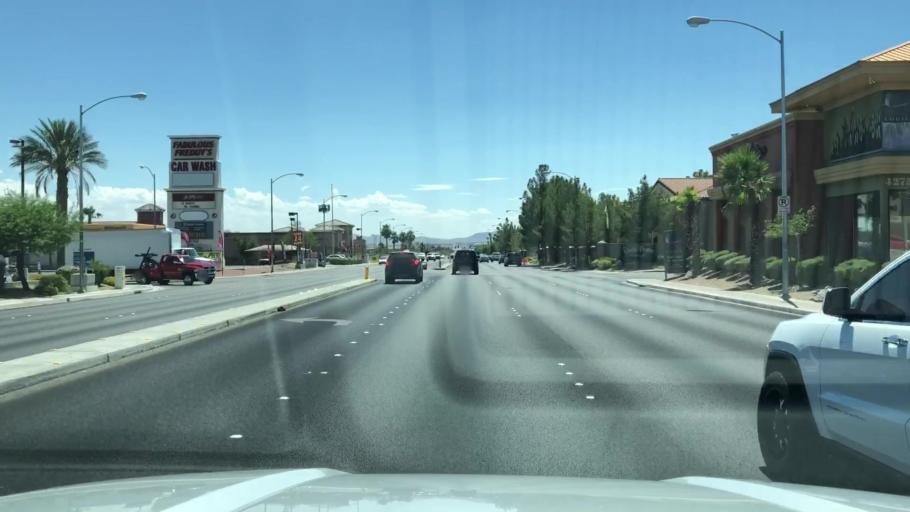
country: US
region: Nevada
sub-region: Clark County
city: Spring Valley
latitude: 36.1117
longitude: -115.2792
